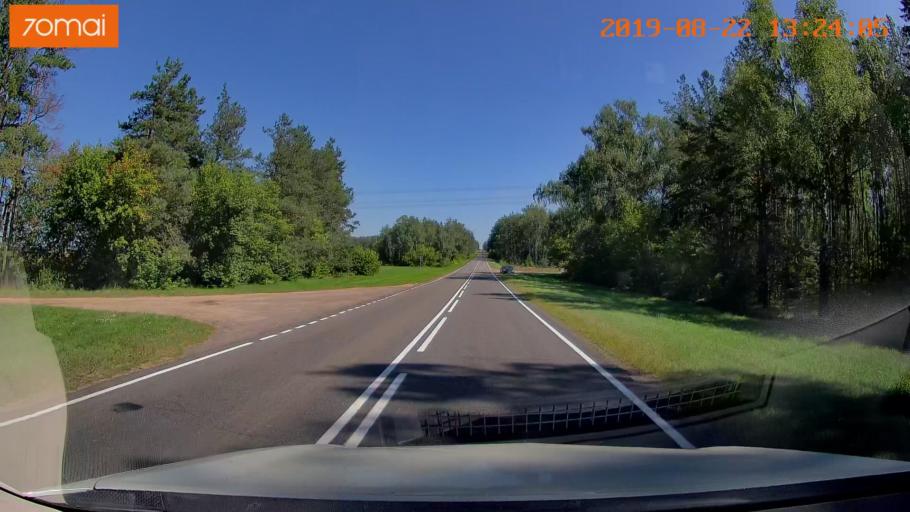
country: BY
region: Minsk
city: Urechcha
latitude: 53.2107
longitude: 28.0132
